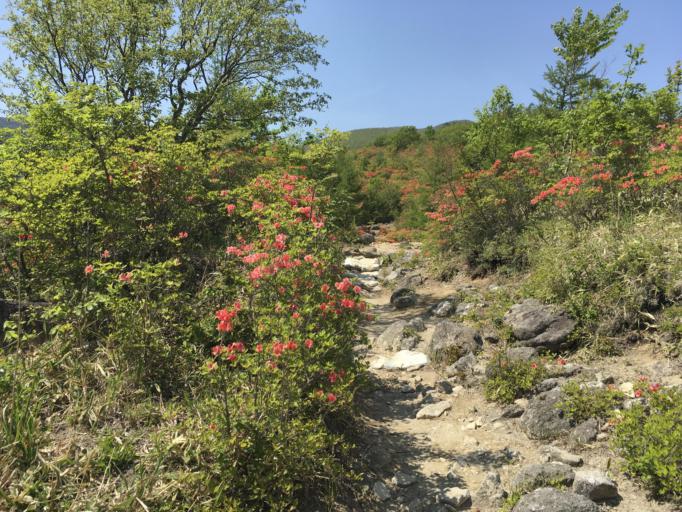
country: JP
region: Iwate
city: Ofunato
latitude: 39.1834
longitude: 141.7349
